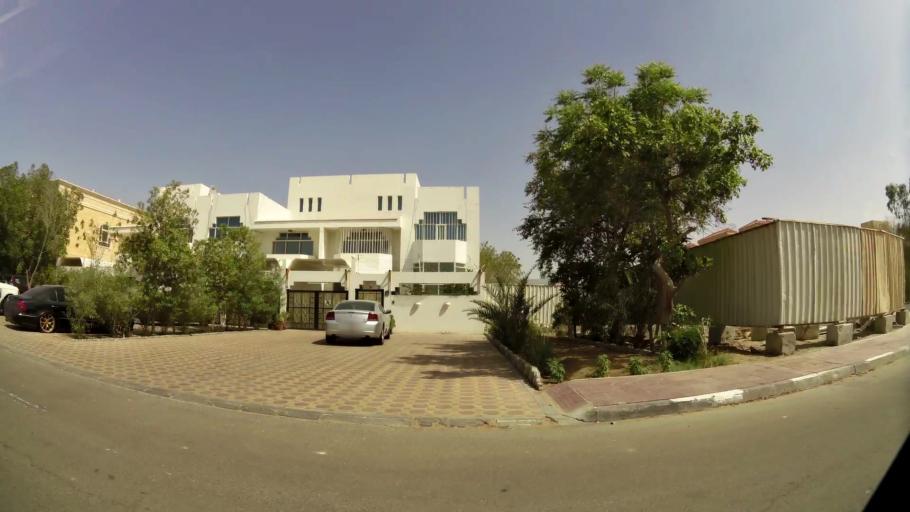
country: AE
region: Abu Dhabi
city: Al Ain
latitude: 24.2214
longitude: 55.6893
